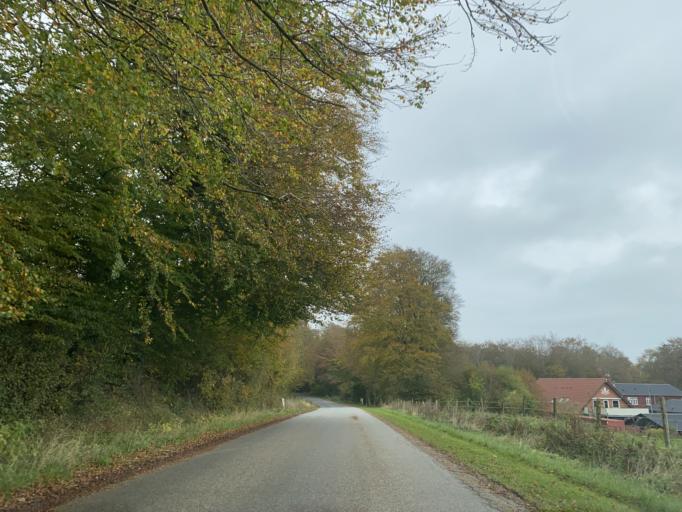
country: DK
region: South Denmark
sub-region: Haderslev Kommune
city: Starup
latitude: 55.1622
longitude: 9.5133
